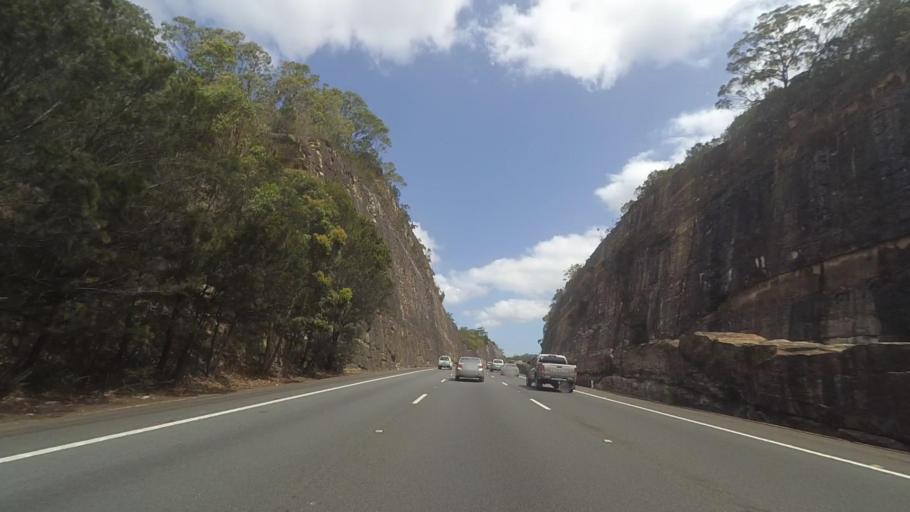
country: AU
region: New South Wales
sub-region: Hornsby Shire
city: Berowra
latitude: -33.5708
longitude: 151.1929
